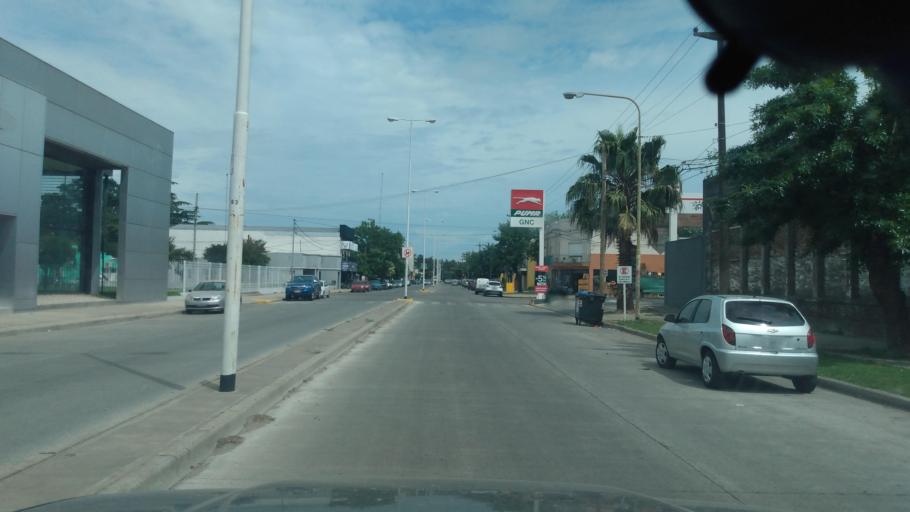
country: AR
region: Buenos Aires
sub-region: Partido de Lujan
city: Lujan
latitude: -34.5619
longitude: -59.1058
